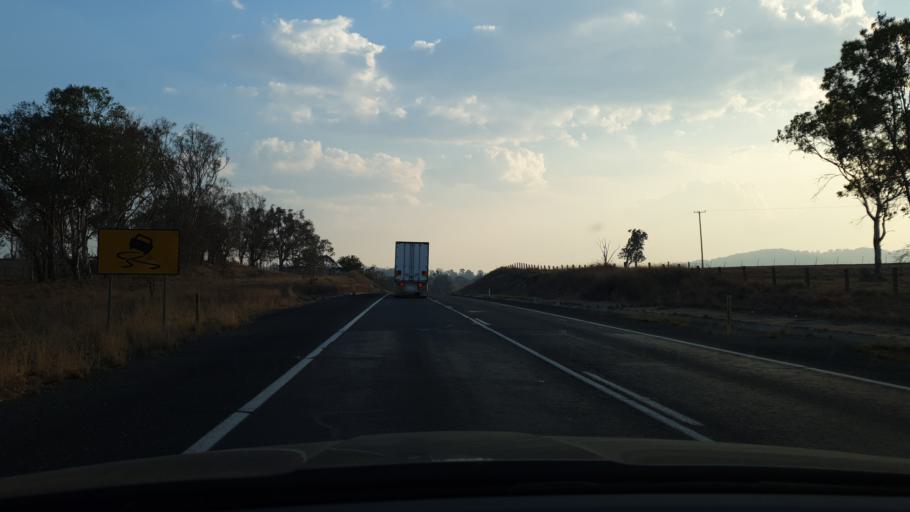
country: AU
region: New South Wales
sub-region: Tenterfield Municipality
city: Carrolls Creek
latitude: -29.1025
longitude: 152.0009
